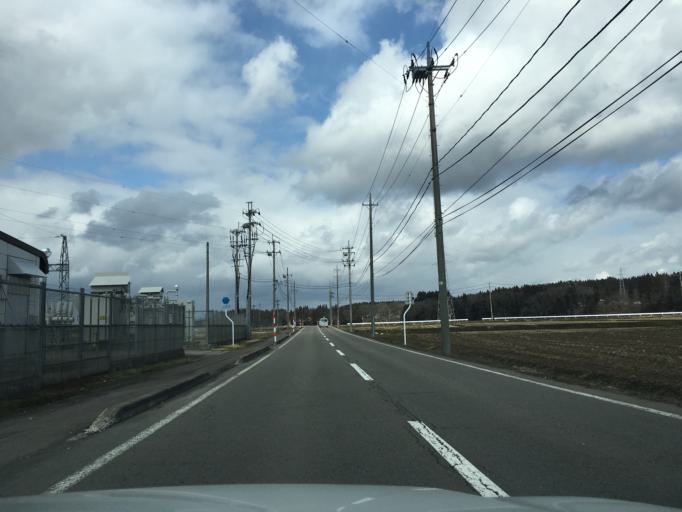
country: JP
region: Akita
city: Takanosu
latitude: 40.1249
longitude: 140.3657
